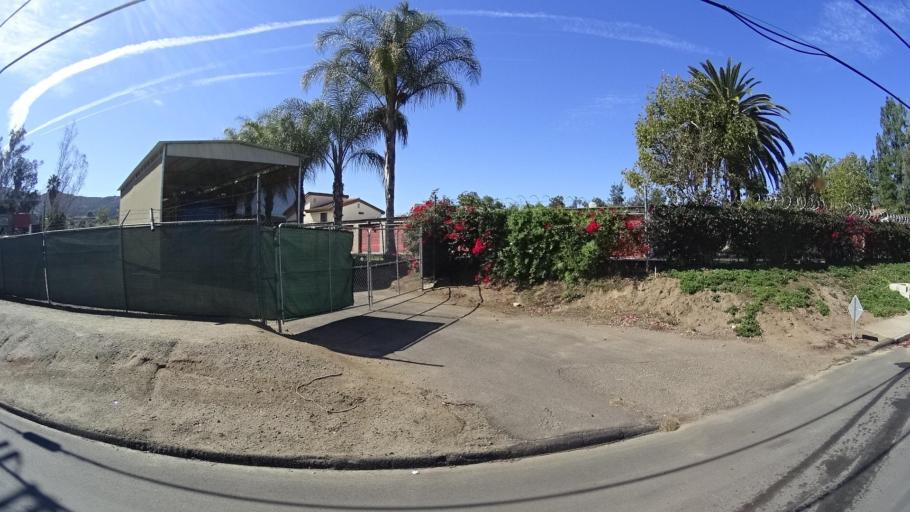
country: US
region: California
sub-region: San Diego County
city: Lakeside
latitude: 32.8410
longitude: -116.8934
